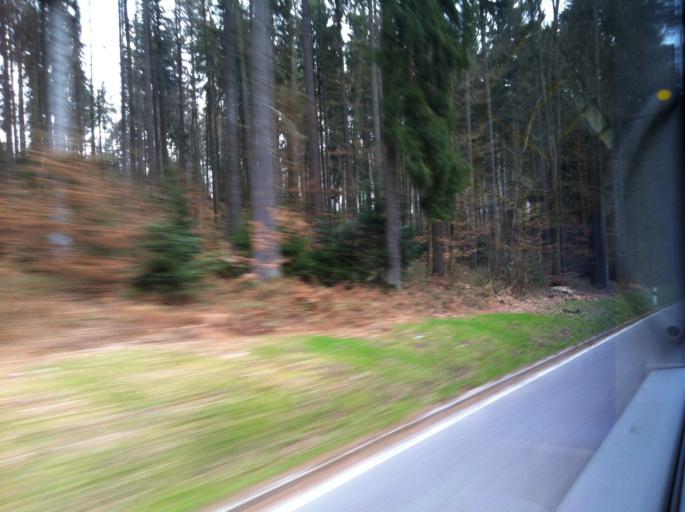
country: DE
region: Baden-Wuerttemberg
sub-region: Karlsruhe Region
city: Fahrenbach
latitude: 49.4405
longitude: 9.1562
